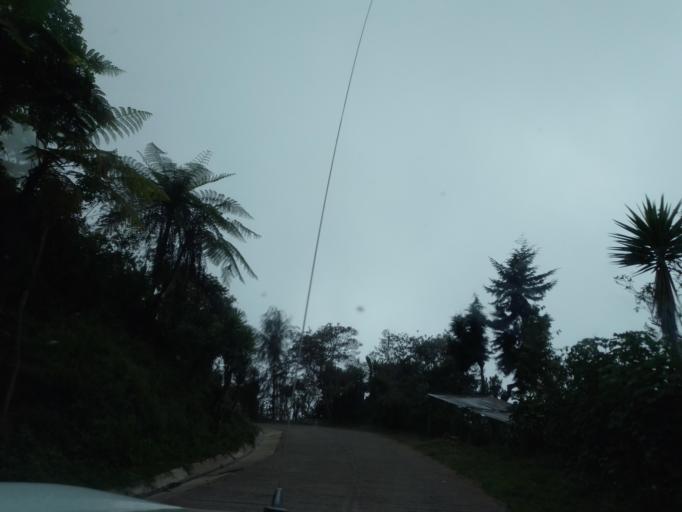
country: MX
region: Chiapas
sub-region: Union Juarez
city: Santo Domingo
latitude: 15.0872
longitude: -92.0909
